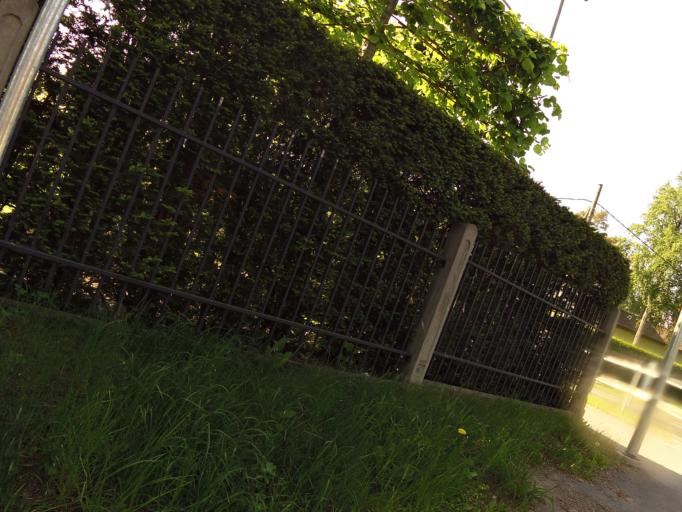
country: EE
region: Harju
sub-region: Harku vald
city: Tabasalu
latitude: 59.4476
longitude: 24.6066
